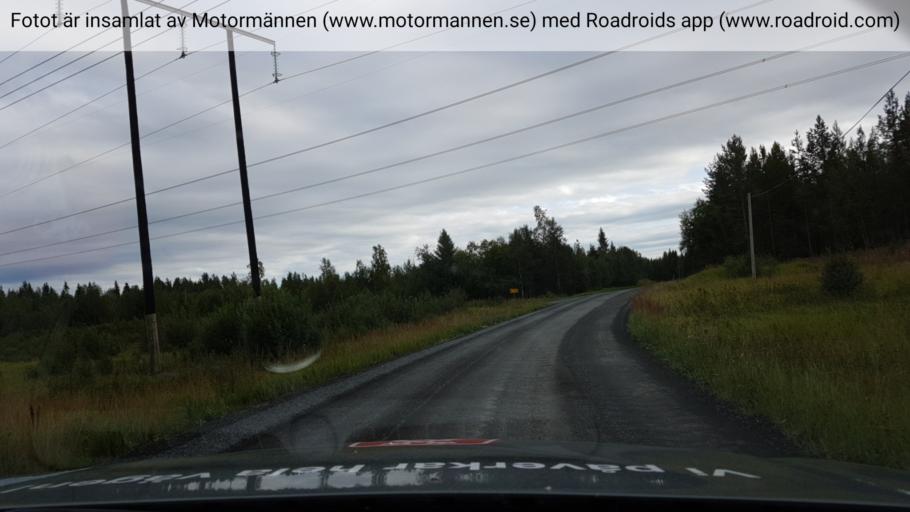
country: SE
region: Jaemtland
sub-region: Krokoms Kommun
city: Valla
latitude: 63.3408
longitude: 14.0107
